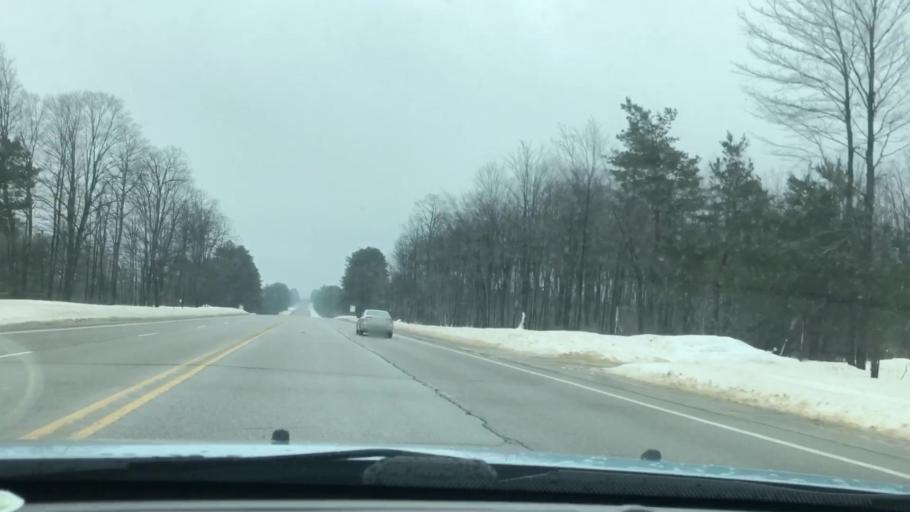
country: US
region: Michigan
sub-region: Otsego County
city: Gaylord
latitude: 45.0621
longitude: -84.8292
